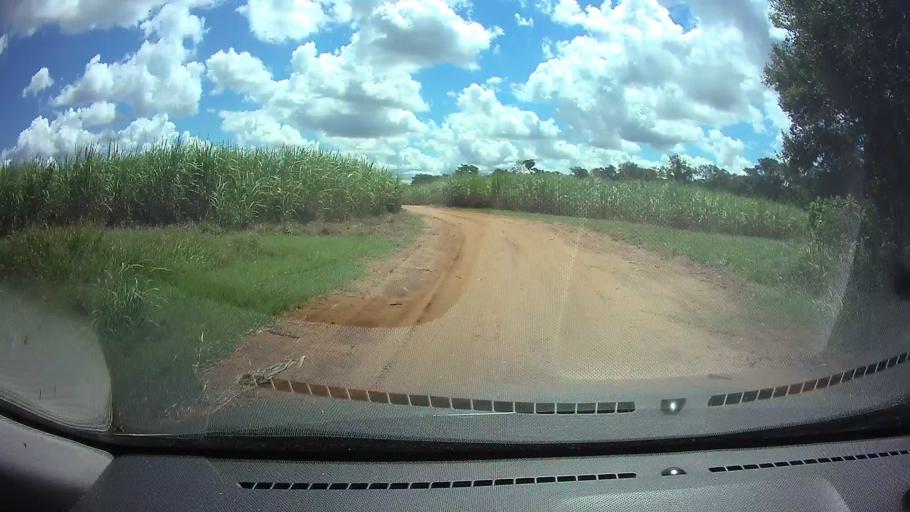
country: PY
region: Paraguari
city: La Colmena
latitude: -25.9508
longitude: -56.7780
